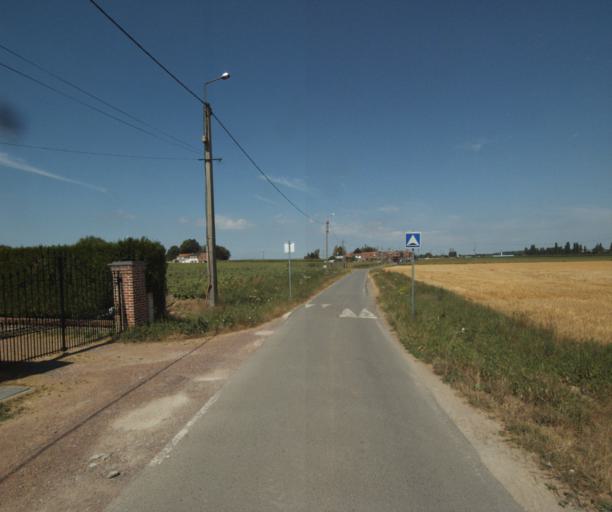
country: FR
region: Nord-Pas-de-Calais
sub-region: Departement du Nord
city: Halluin
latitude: 50.7759
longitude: 3.1510
